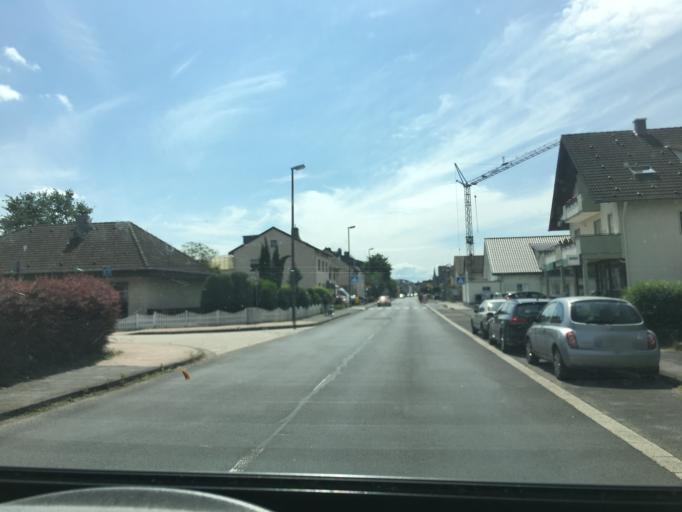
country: DE
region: Rheinland-Pfalz
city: Ockenfels
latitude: 50.5649
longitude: 7.2643
